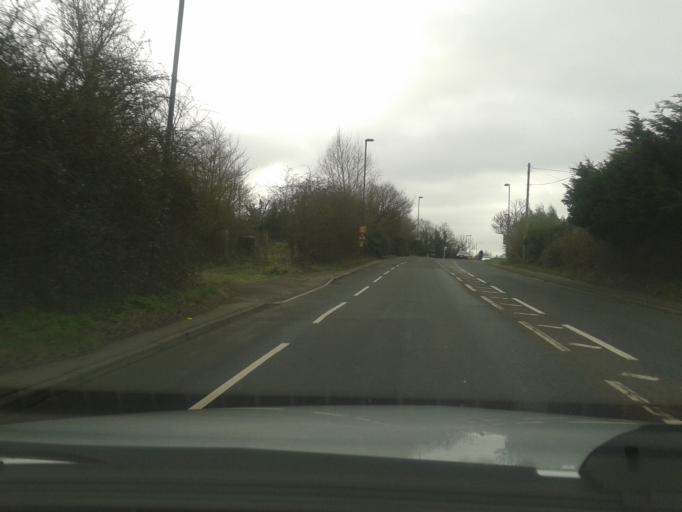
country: GB
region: England
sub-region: South Gloucestershire
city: Winterbourne
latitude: 51.5138
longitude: -2.4863
